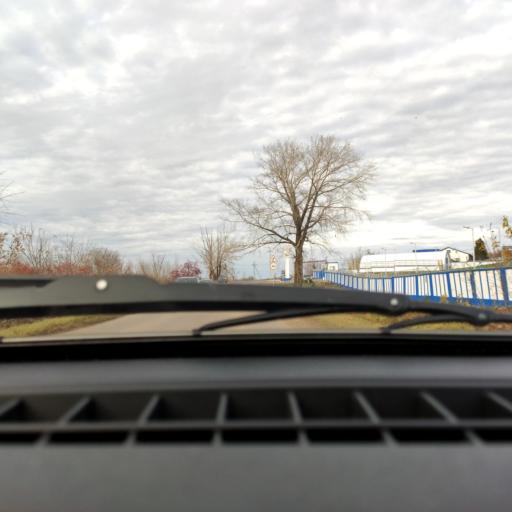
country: RU
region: Bashkortostan
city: Ufa
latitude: 54.8756
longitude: 56.1292
